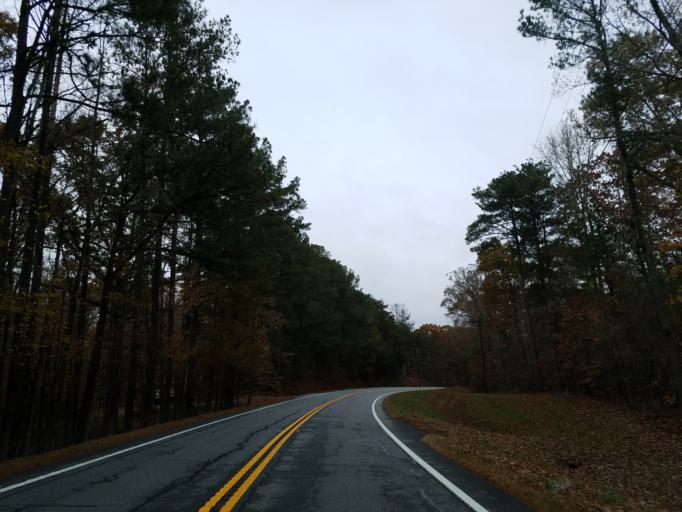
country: US
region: Georgia
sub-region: Cherokee County
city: Canton
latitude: 34.2491
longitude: -84.6057
